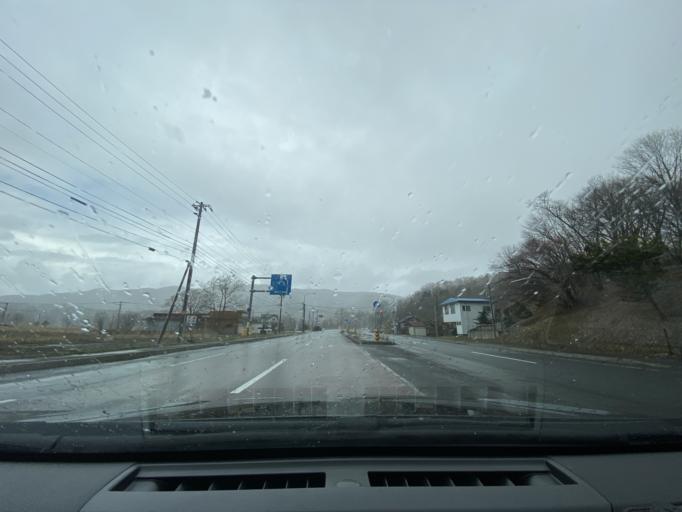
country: JP
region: Hokkaido
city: Fukagawa
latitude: 43.7266
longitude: 142.1869
